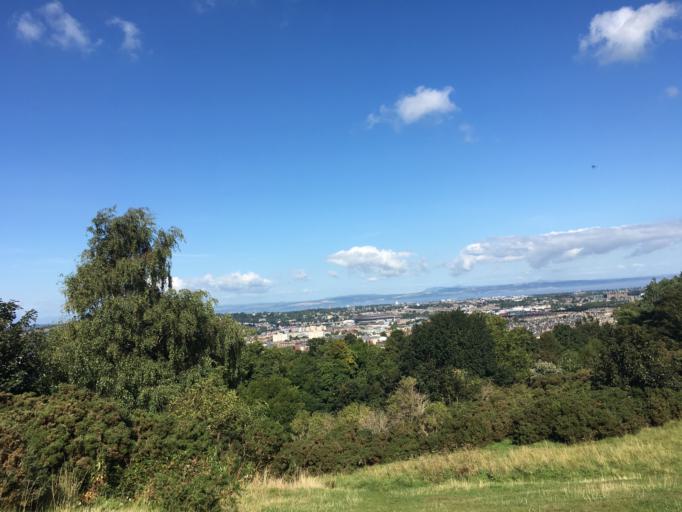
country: GB
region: Scotland
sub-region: Edinburgh
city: Colinton
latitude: 55.9215
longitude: -3.2316
